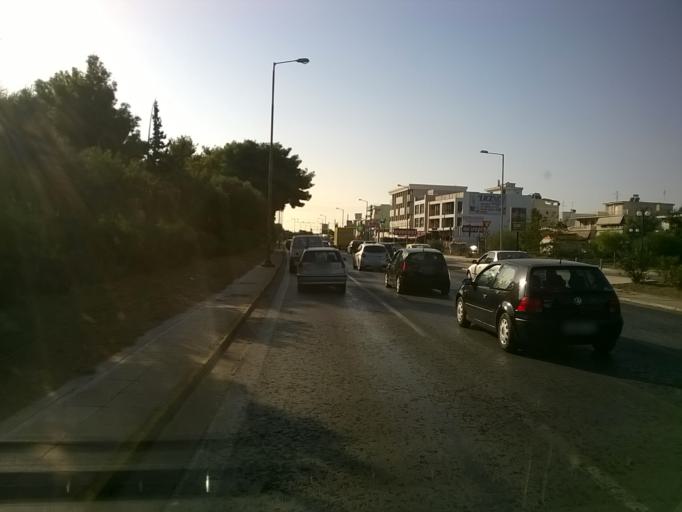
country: GR
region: Attica
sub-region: Nomarchia Athinas
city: Elliniko
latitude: 37.8884
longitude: 23.7494
